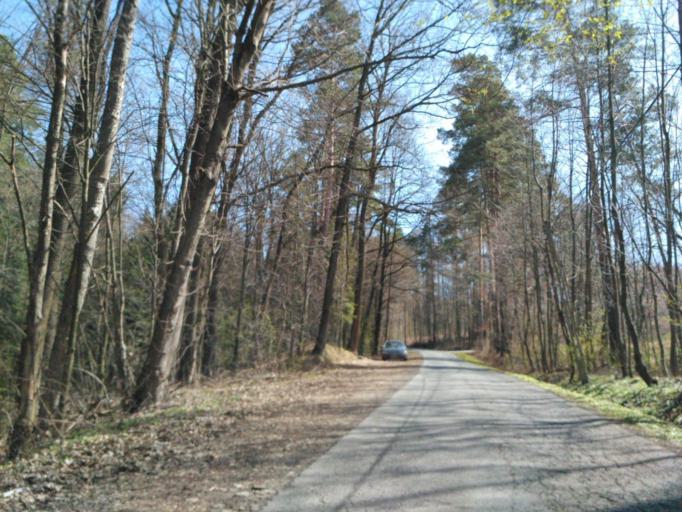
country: PL
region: Subcarpathian Voivodeship
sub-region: Powiat strzyzowski
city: Babica
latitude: 49.9249
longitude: 21.8868
